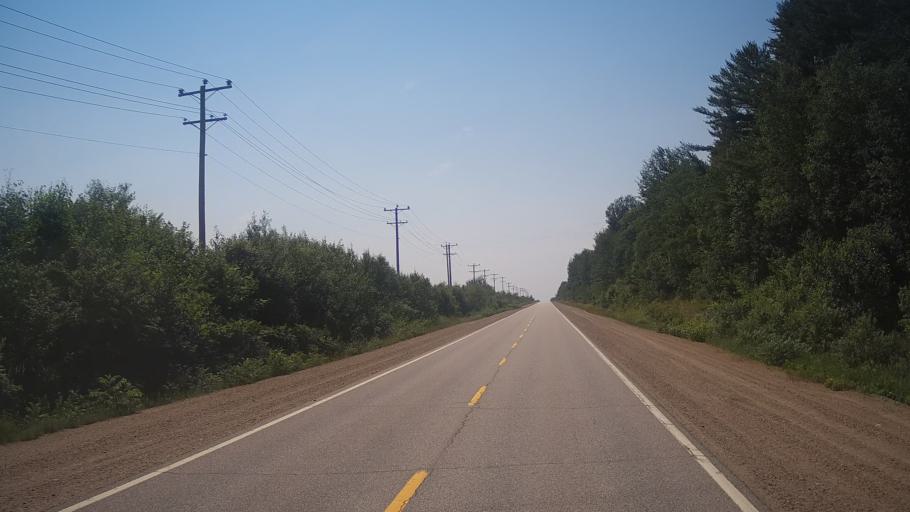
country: CA
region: Ontario
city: Pembroke
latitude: 45.8807
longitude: -76.9576
